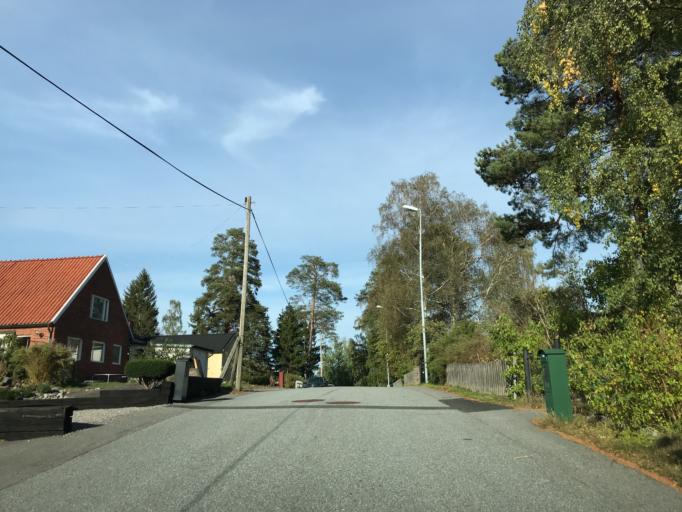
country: SE
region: Stockholm
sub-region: Sollentuna Kommun
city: Sollentuna
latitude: 59.4229
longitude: 17.9393
